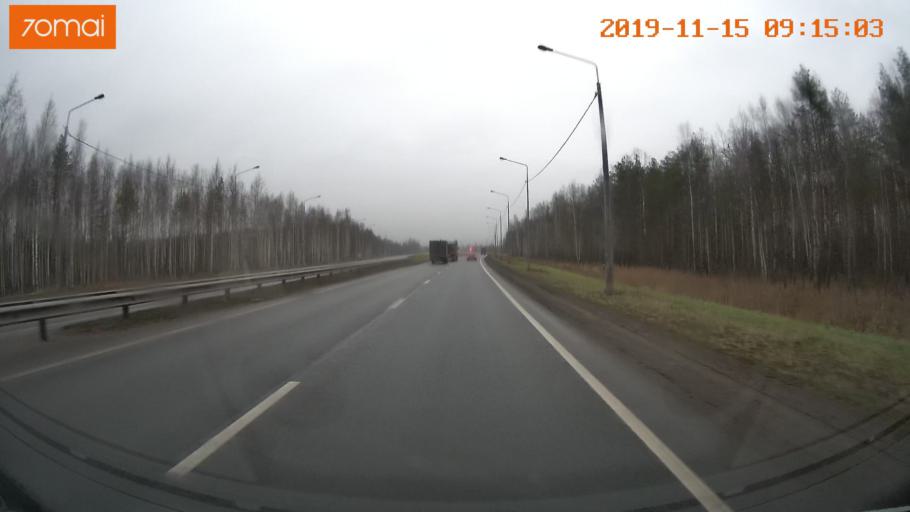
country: RU
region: Vologda
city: Tonshalovo
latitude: 59.2341
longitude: 37.9640
